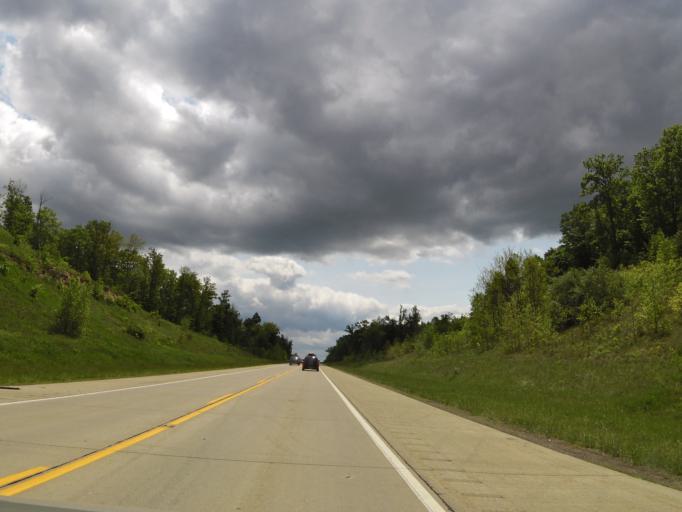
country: US
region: Ohio
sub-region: Meigs County
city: Pomeroy
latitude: 39.1657
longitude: -82.0392
